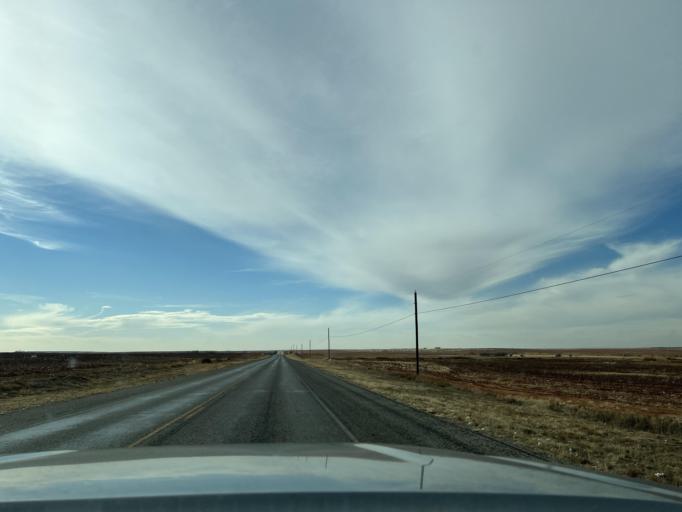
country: US
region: Texas
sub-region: Fisher County
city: Roby
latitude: 32.7414
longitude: -100.4614
